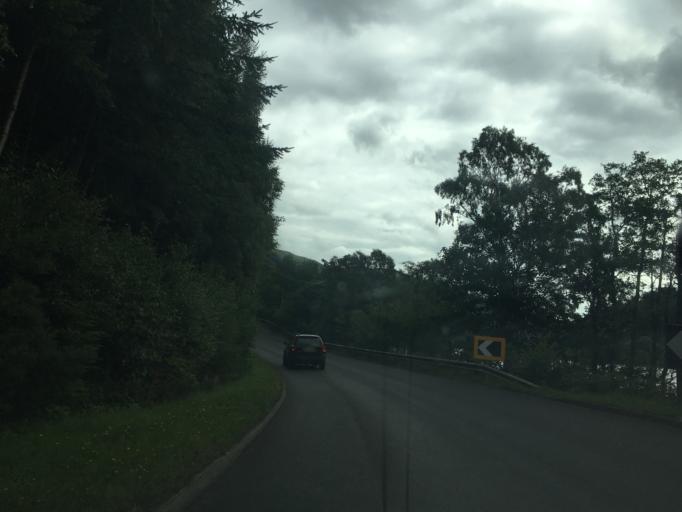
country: GB
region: Scotland
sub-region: Stirling
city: Callander
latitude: 56.2968
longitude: -4.3025
